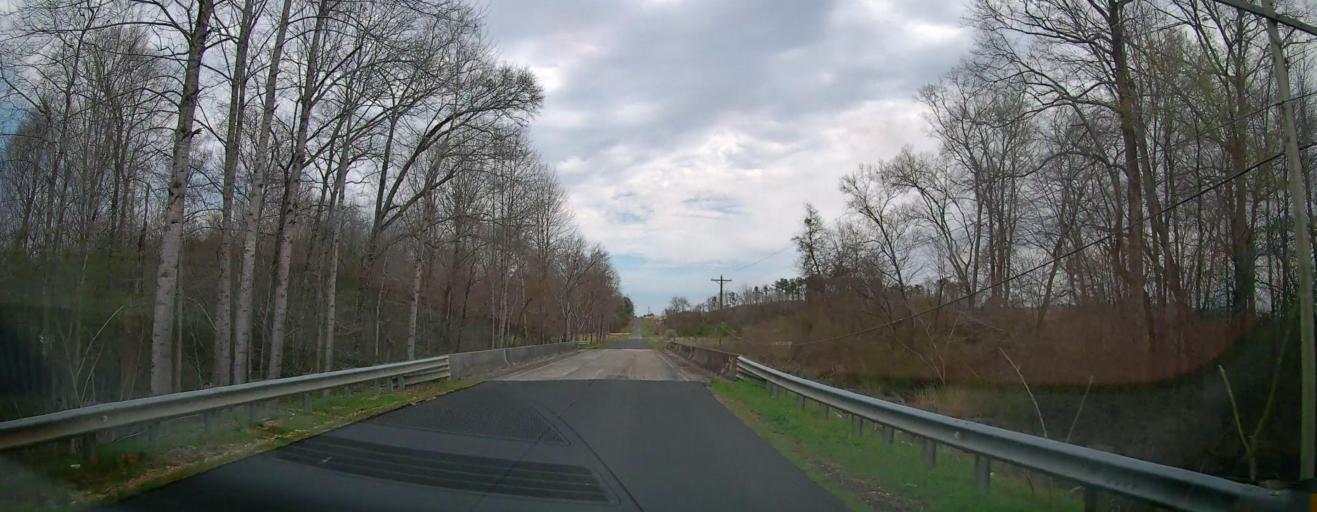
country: US
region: Alabama
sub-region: Marion County
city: Hamilton
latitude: 34.1864
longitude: -88.1403
